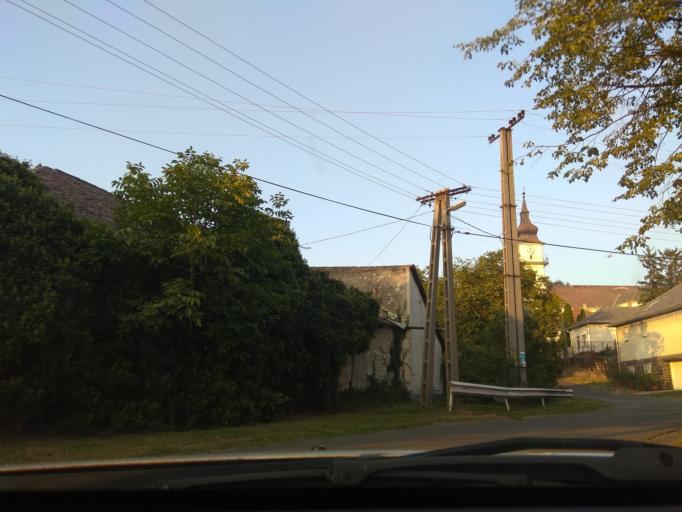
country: HU
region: Borsod-Abauj-Zemplen
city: Tallya
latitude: 48.2337
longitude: 21.2297
